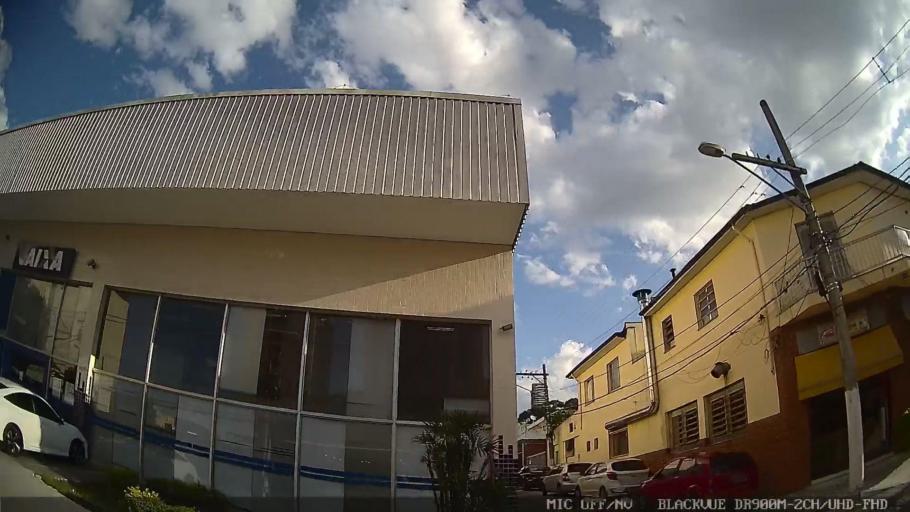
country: BR
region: Sao Paulo
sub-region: Sao Paulo
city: Sao Paulo
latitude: -23.5440
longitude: -46.5630
